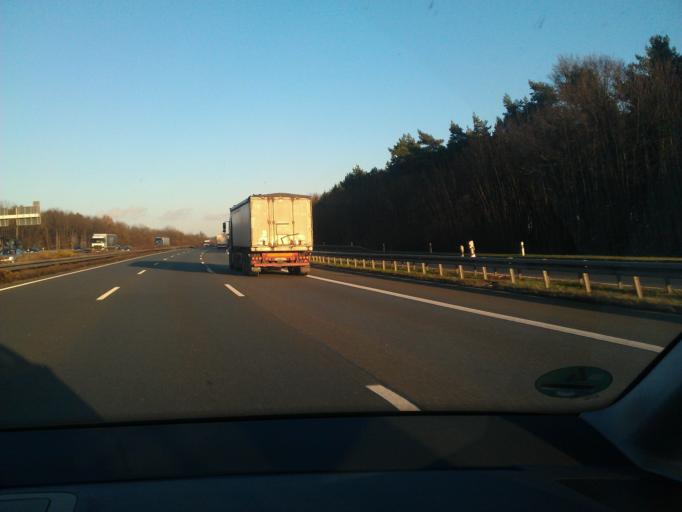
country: DE
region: North Rhine-Westphalia
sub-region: Regierungsbezirk Detmold
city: Rheda-Wiedenbruck
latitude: 51.8558
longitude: 8.3262
